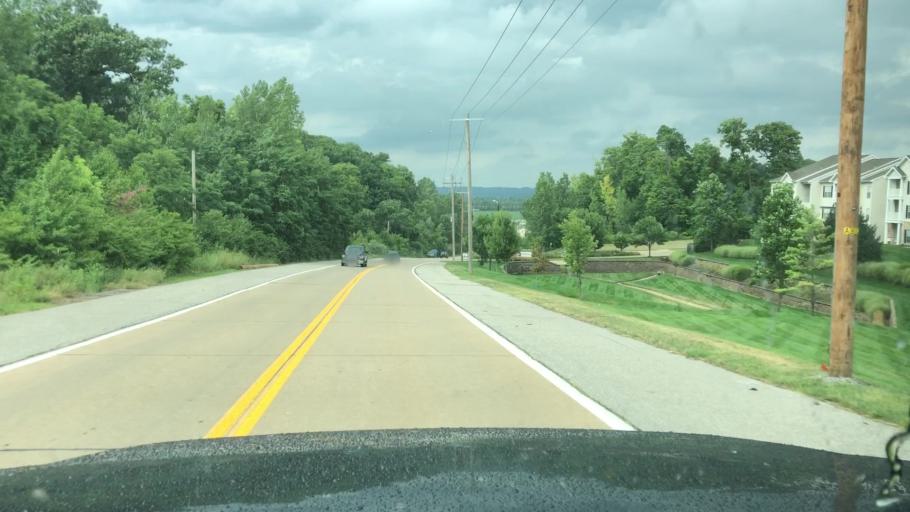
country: US
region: Missouri
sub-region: Saint Charles County
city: Saint Peters
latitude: 38.7998
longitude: -90.5805
